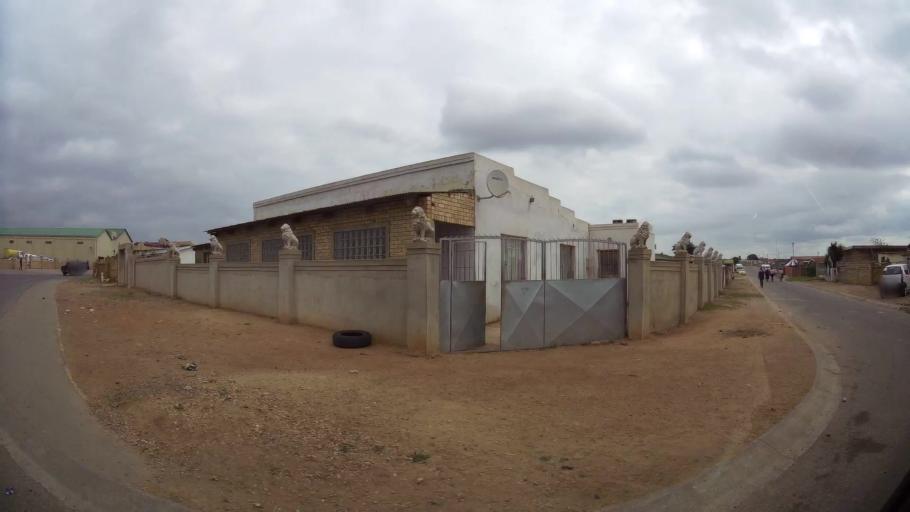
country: ZA
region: Eastern Cape
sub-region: Nelson Mandela Bay Metropolitan Municipality
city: Port Elizabeth
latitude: -33.8767
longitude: 25.5647
